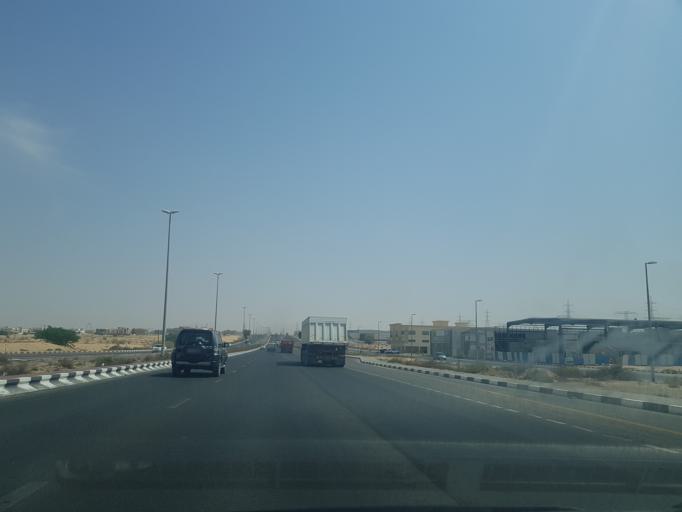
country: AE
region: Ash Shariqah
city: Sharjah
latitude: 25.2486
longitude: 55.5391
